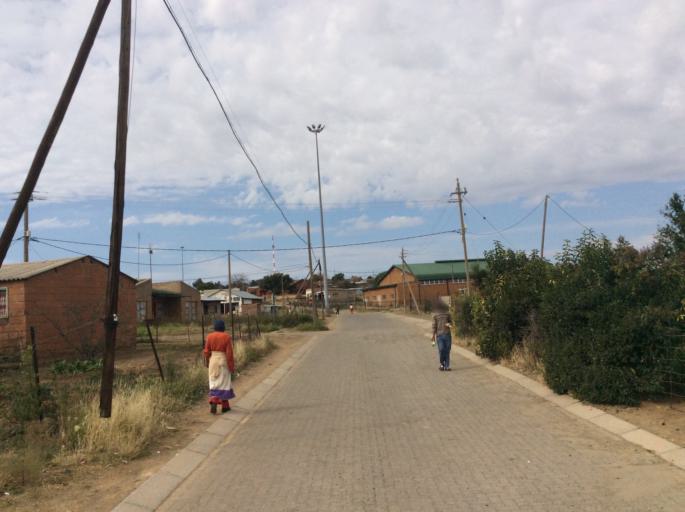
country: LS
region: Mafeteng
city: Mafeteng
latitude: -29.7187
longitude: 27.0265
